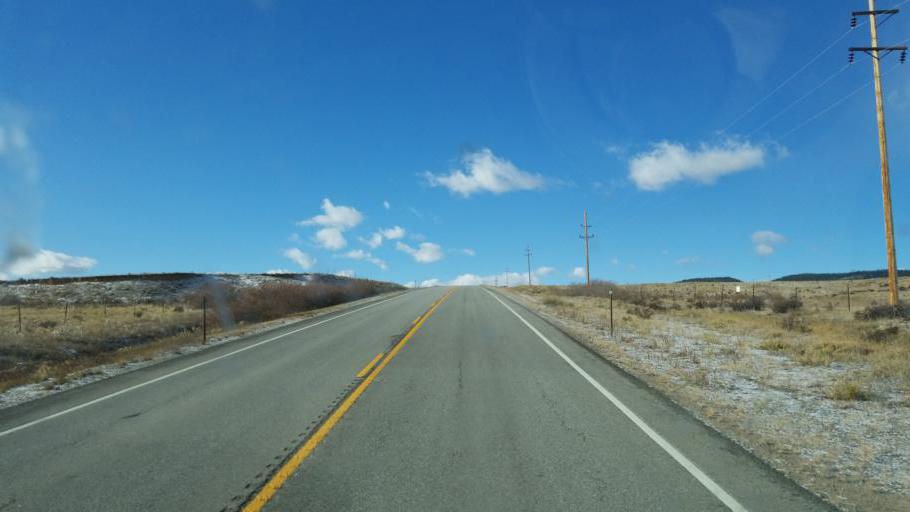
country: US
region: Colorado
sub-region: Park County
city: Fairplay
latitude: 39.3310
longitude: -105.8687
